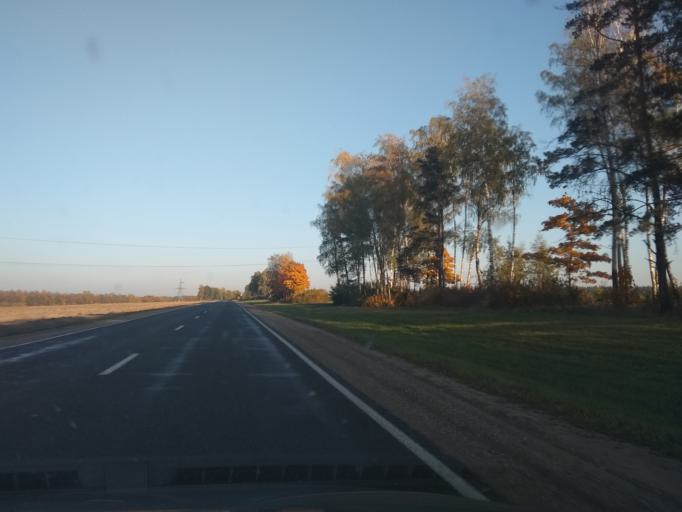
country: BY
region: Grodnenskaya
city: Vawkavysk
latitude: 53.1495
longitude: 24.5471
